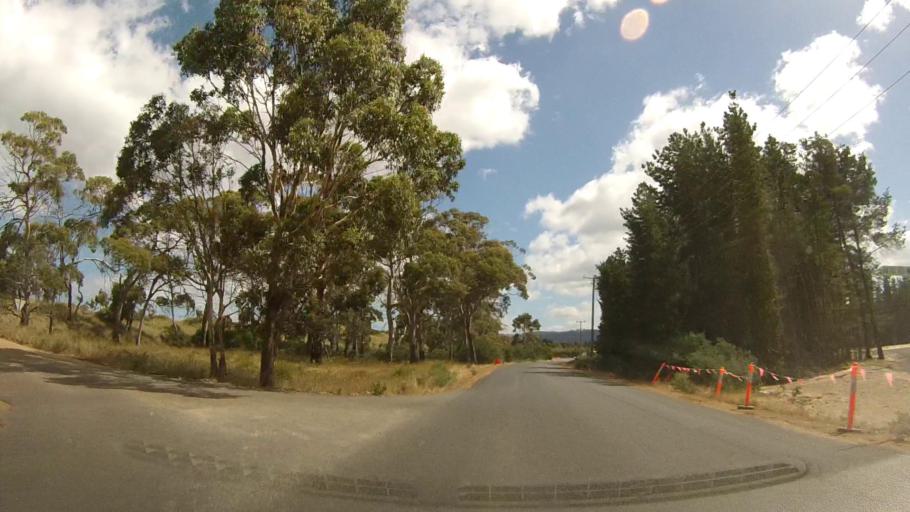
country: AU
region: Tasmania
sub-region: Clarence
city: Seven Mile Beach
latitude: -42.8500
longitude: 147.5197
